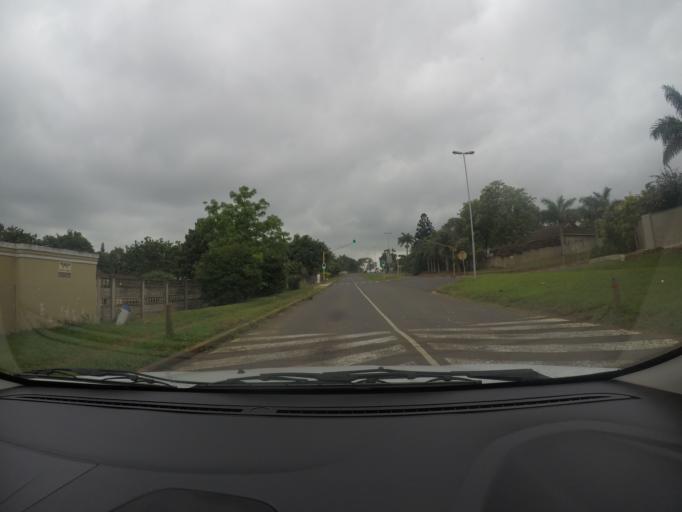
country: ZA
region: KwaZulu-Natal
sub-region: uThungulu District Municipality
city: Empangeni
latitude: -28.7676
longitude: 31.8950
